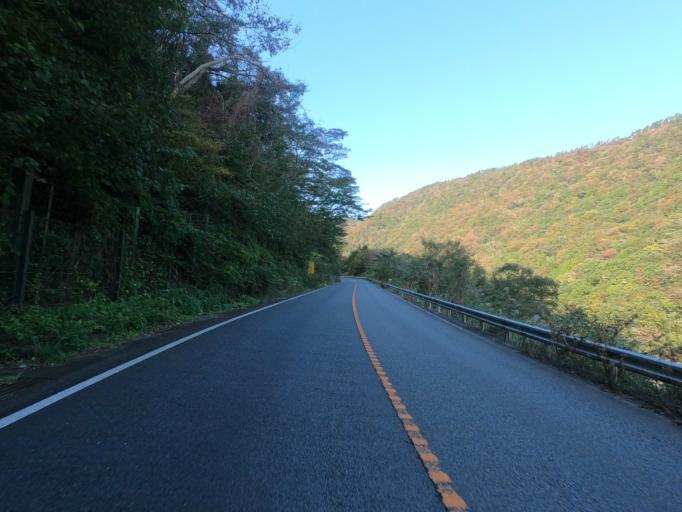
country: JP
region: Kanagawa
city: Hakone
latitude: 35.2224
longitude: 139.0856
